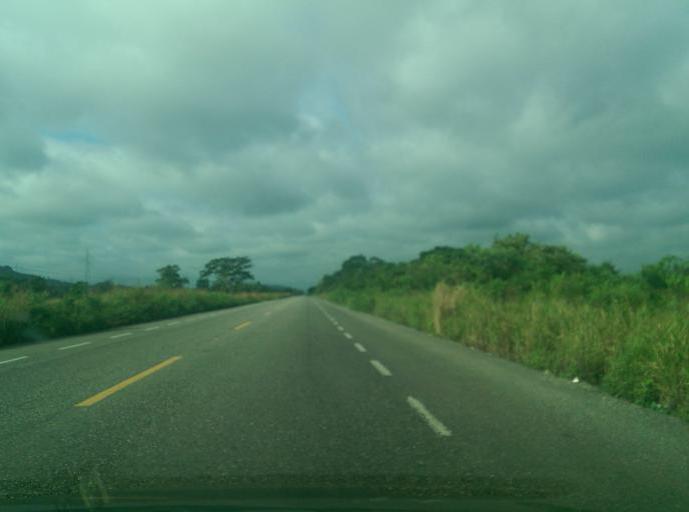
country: MX
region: Tabasco
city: Aquiles Serdan
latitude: 17.6927
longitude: -92.3192
